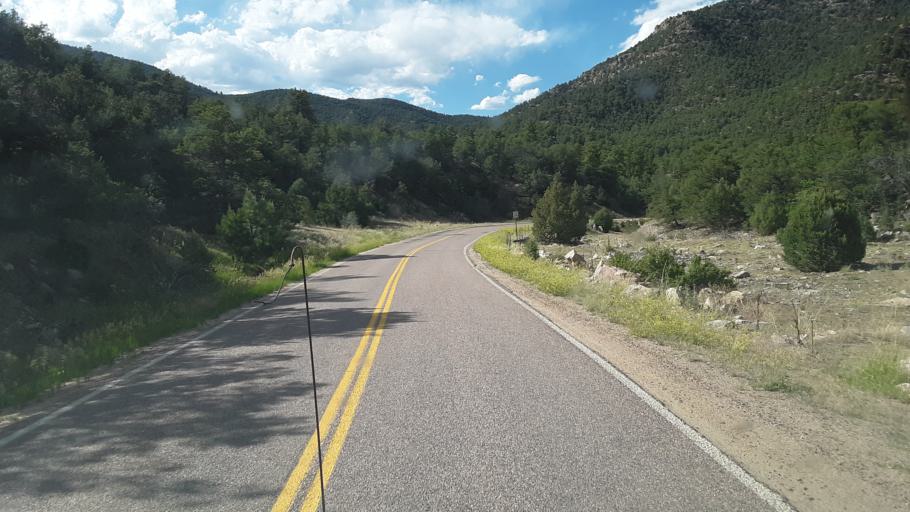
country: US
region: Colorado
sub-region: Fremont County
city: Canon City
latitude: 38.4104
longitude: -105.4369
